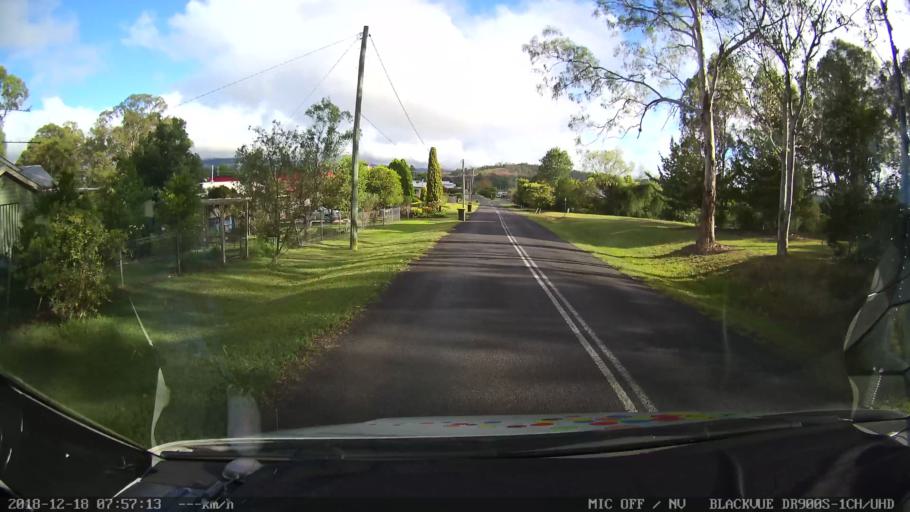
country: AU
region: New South Wales
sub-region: Kyogle
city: Kyogle
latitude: -28.3950
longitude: 152.6111
